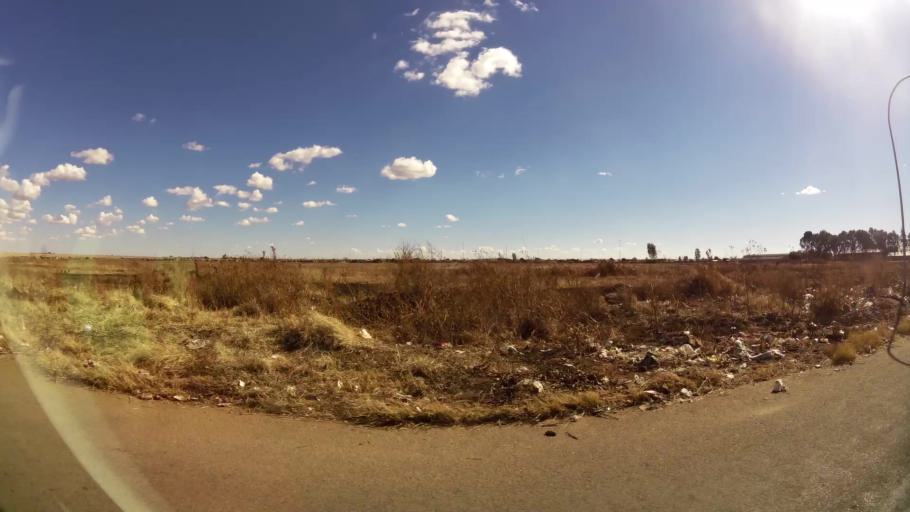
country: ZA
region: North-West
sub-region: Dr Kenneth Kaunda District Municipality
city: Klerksdorp
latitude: -26.8745
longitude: 26.5803
